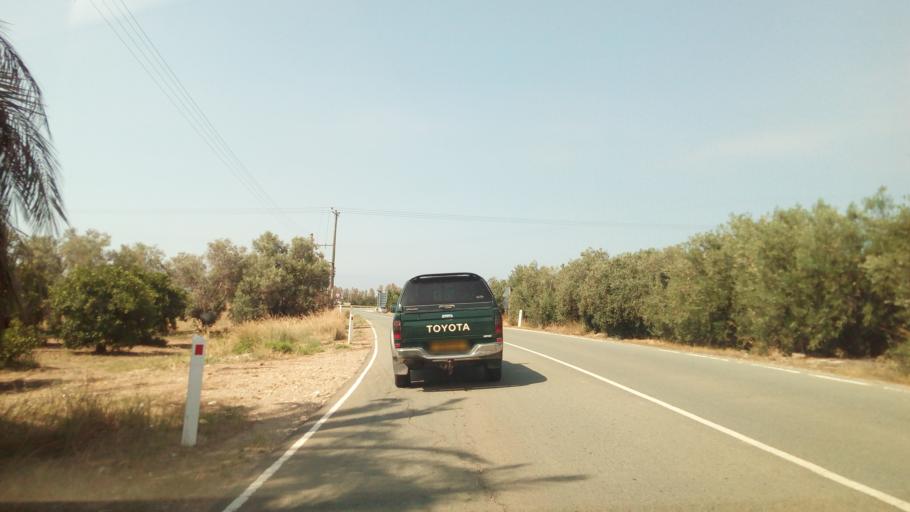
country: CY
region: Pafos
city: Mesogi
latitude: 34.7162
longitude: 32.5510
